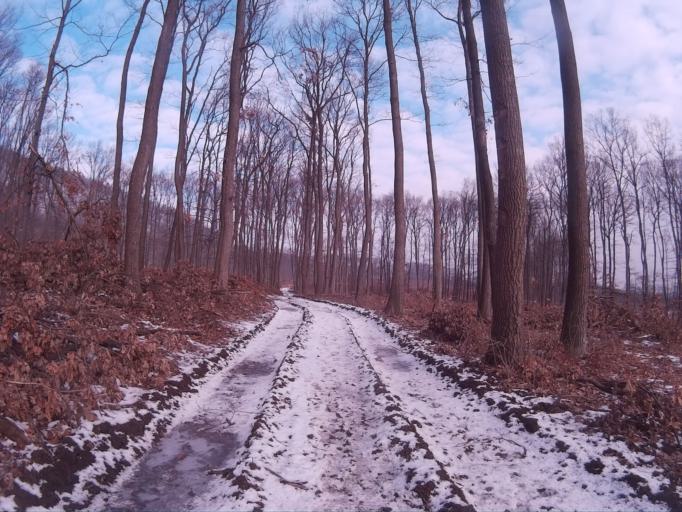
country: HU
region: Komarom-Esztergom
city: Tardos
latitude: 47.6724
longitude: 18.5049
